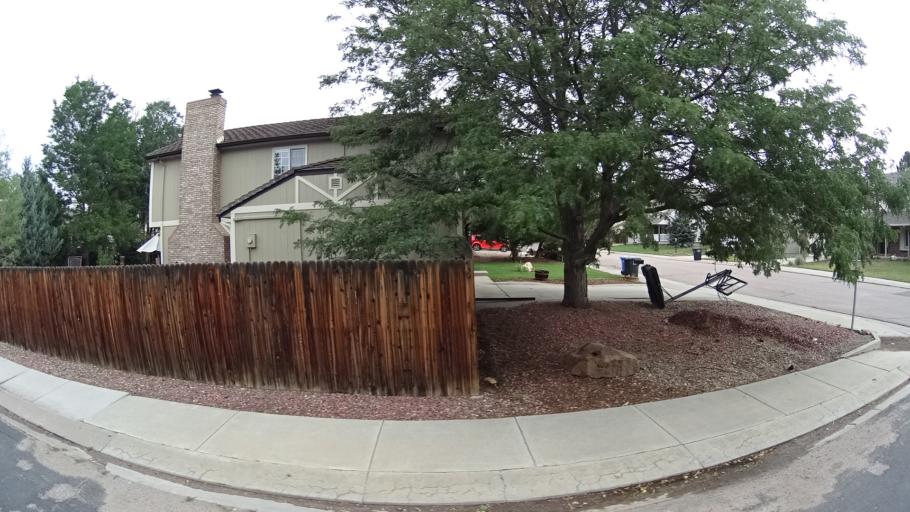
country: US
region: Colorado
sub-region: El Paso County
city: Air Force Academy
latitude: 38.9224
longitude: -104.8338
